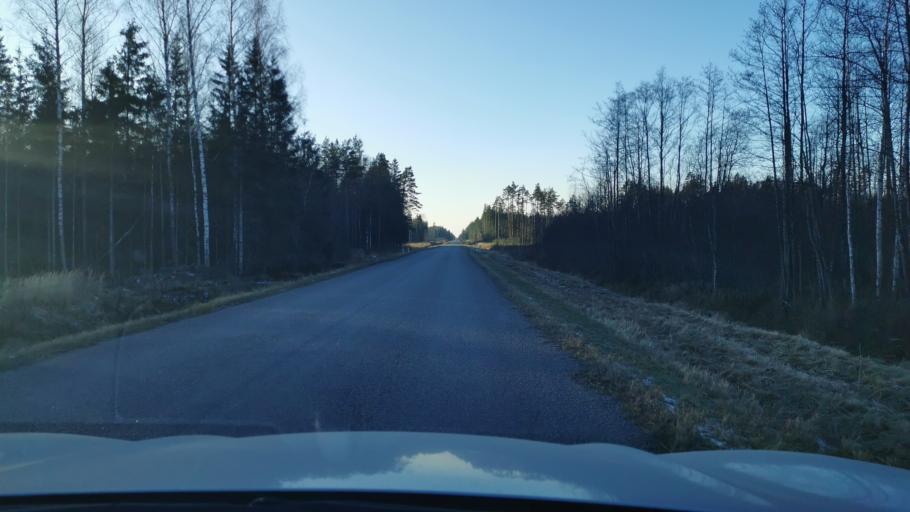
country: EE
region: Ida-Virumaa
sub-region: Kivioli linn
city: Kivioli
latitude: 59.2409
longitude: 26.9853
